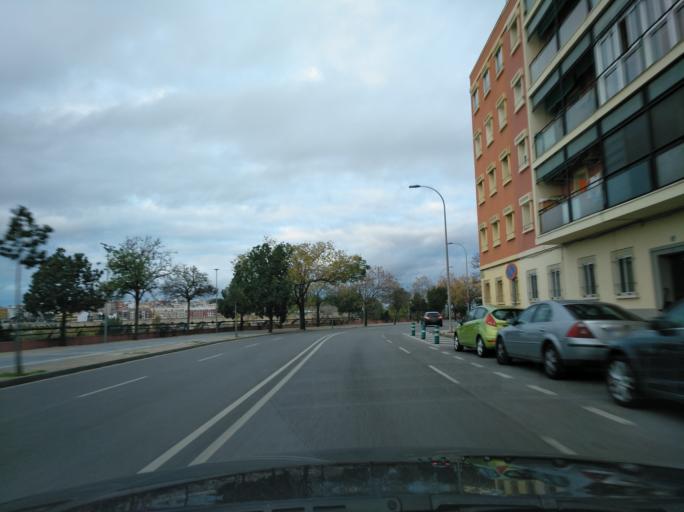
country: ES
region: Extremadura
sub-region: Provincia de Badajoz
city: Badajoz
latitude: 38.8791
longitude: -6.9796
